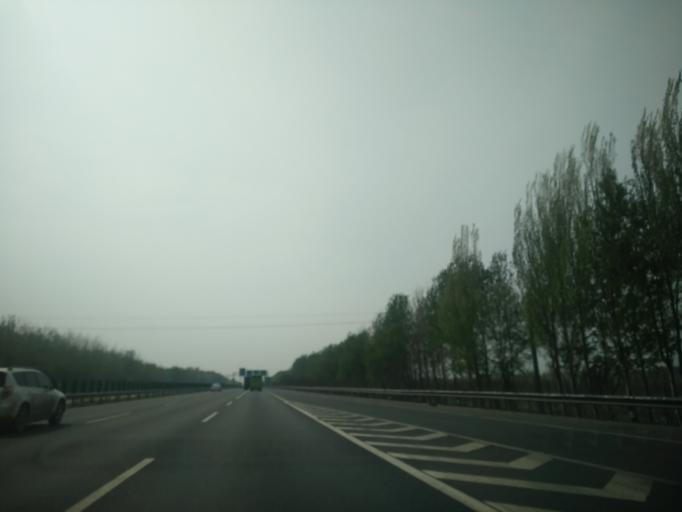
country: CN
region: Beijing
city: Xiji
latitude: 39.7991
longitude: 116.9223
